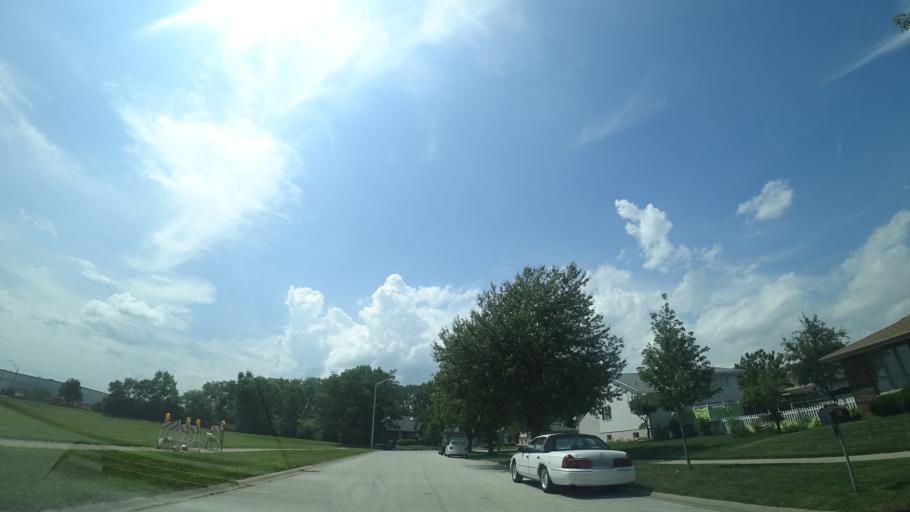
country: US
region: Illinois
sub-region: Cook County
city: Crestwood
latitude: 41.6715
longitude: -87.7509
